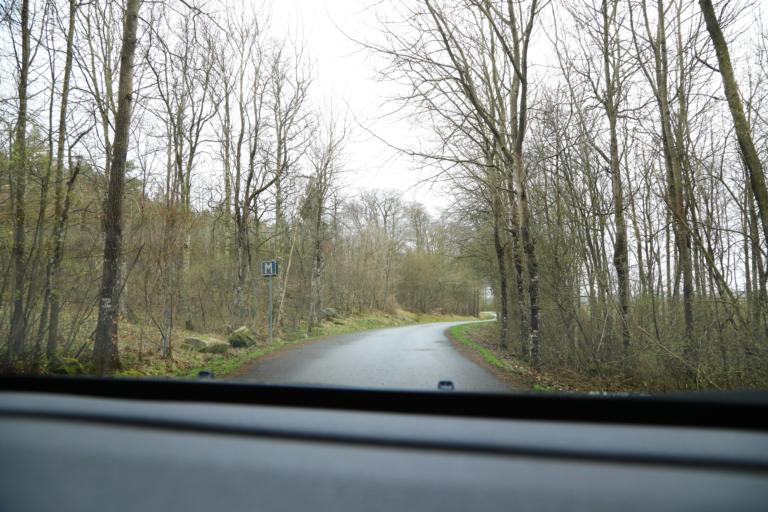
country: SE
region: Halland
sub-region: Kungsbacka Kommun
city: Frillesas
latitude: 57.3085
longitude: 12.1768
